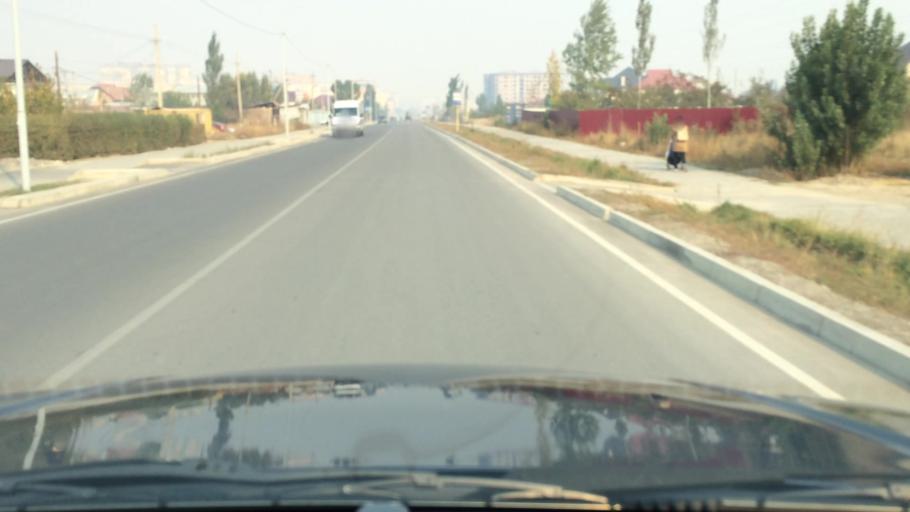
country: KG
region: Chuy
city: Bishkek
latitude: 42.8237
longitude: 74.5699
